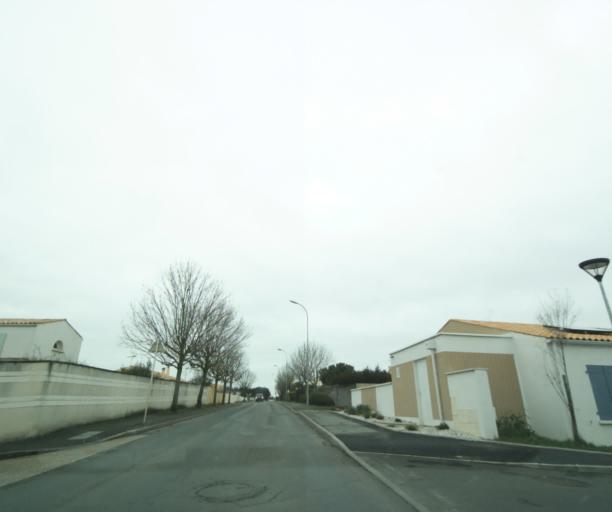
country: FR
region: Poitou-Charentes
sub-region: Departement de la Charente-Maritime
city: Lagord
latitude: 46.1893
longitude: -1.1411
